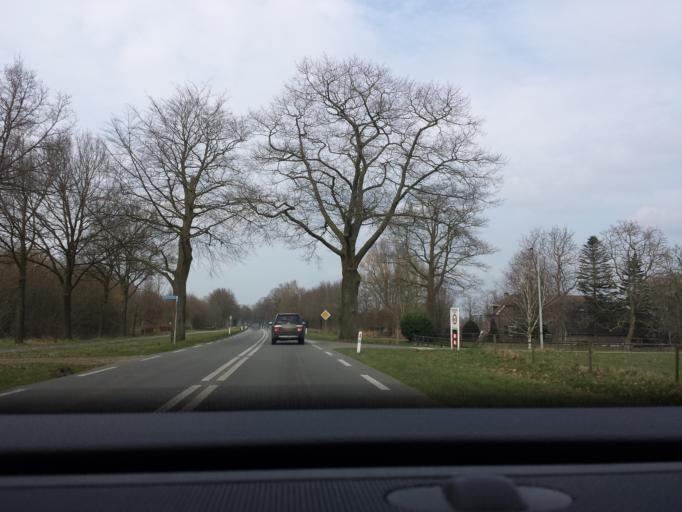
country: NL
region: Gelderland
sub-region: Gemeente Bronckhorst
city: Hengelo
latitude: 52.0631
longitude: 6.3081
